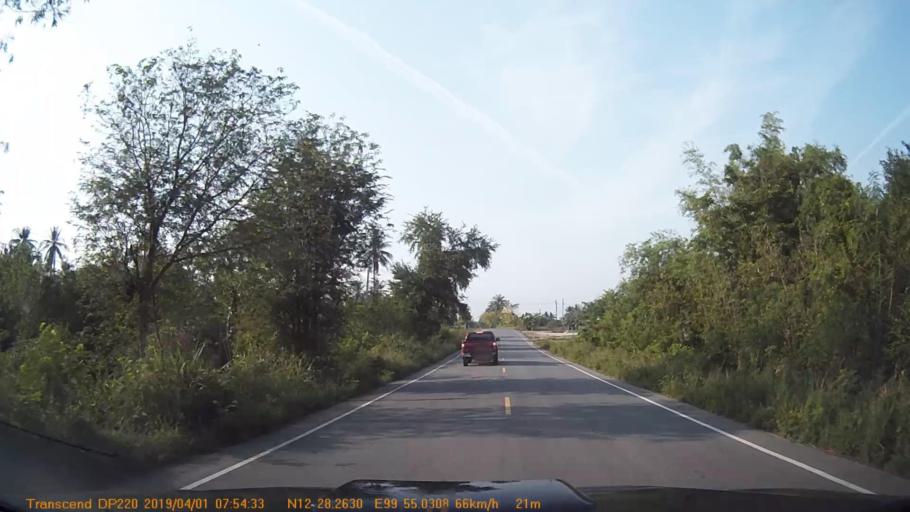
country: TH
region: Prachuap Khiri Khan
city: Pran Buri
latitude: 12.4707
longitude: 99.9172
